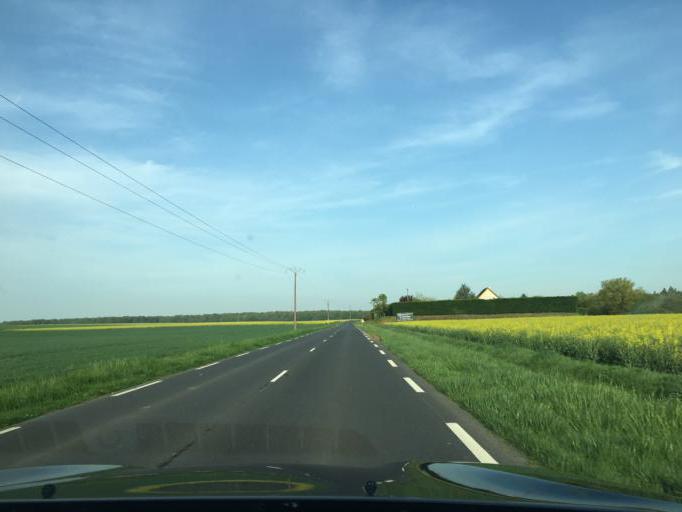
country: FR
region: Ile-de-France
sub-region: Departement des Yvelines
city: Gazeran
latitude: 48.5793
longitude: 1.7624
